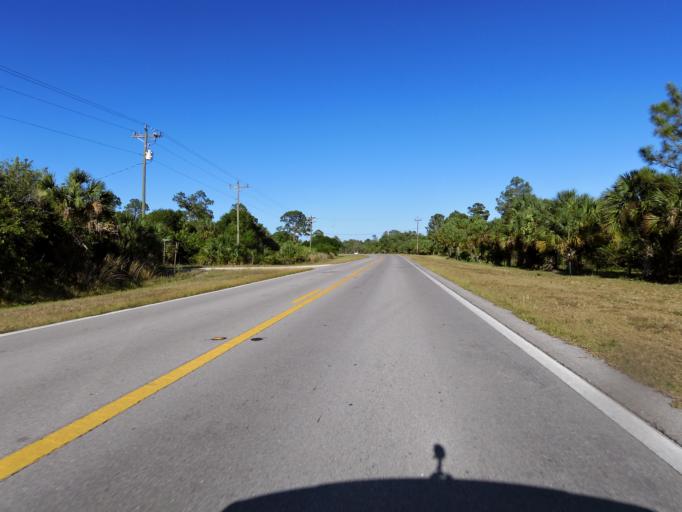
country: US
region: Florida
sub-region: Collier County
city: Immokalee
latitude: 26.2955
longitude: -81.3681
